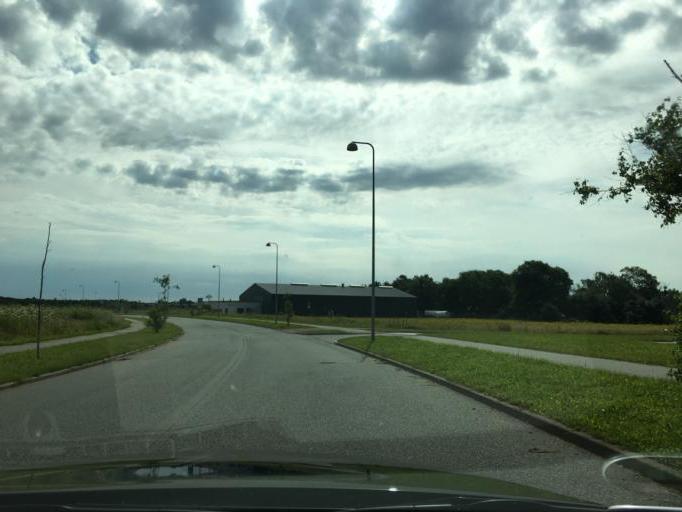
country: DK
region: South Denmark
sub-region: Kolding Kommune
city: Kolding
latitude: 55.5417
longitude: 9.4640
